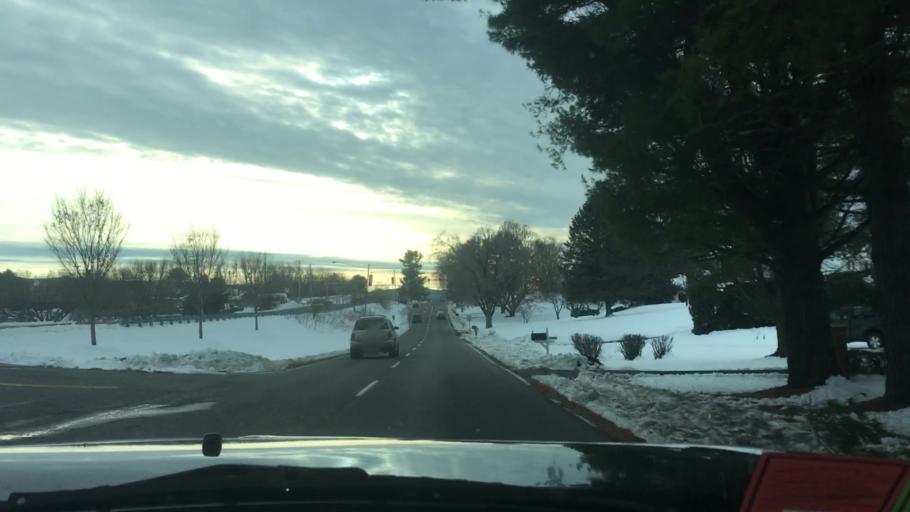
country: US
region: Virginia
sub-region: Pulaski County
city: Pulaski
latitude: 37.0677
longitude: -80.7608
